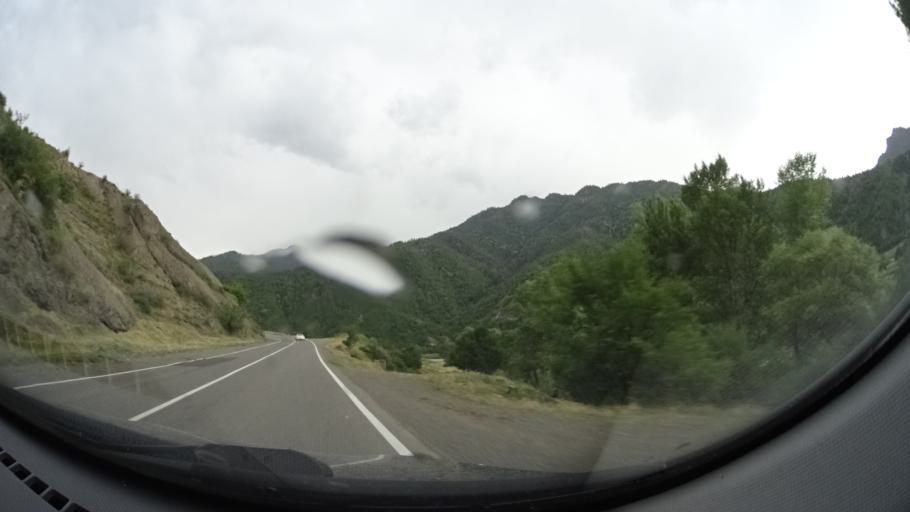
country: GE
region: Samtskhe-Javakheti
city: Borjomi
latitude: 41.7750
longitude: 43.2831
